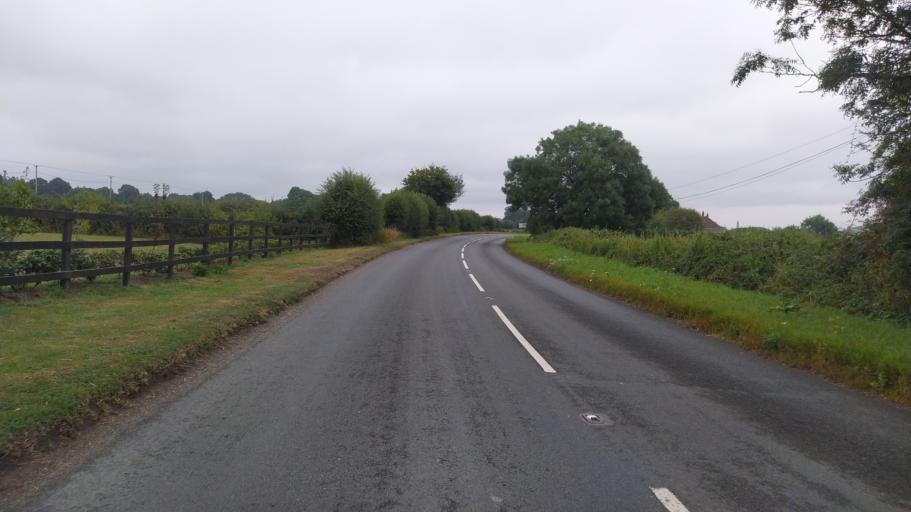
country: GB
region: England
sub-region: Wiltshire
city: Ansty
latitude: 51.0478
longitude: -2.0310
